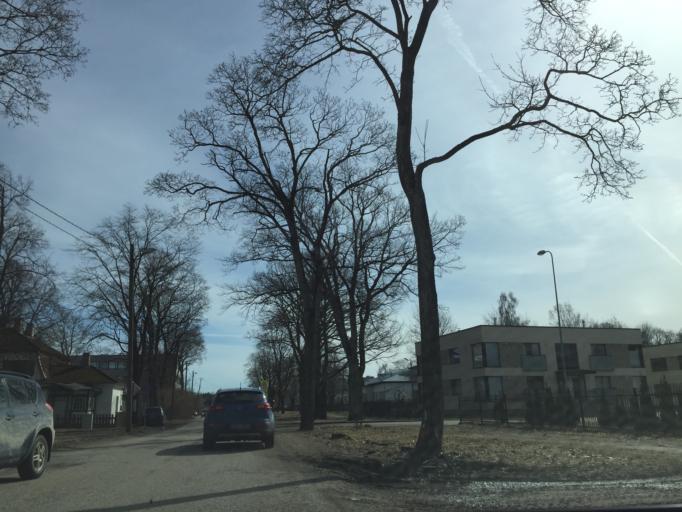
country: EE
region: Paernumaa
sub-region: Paernu linn
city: Parnu
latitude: 58.3832
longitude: 24.5270
